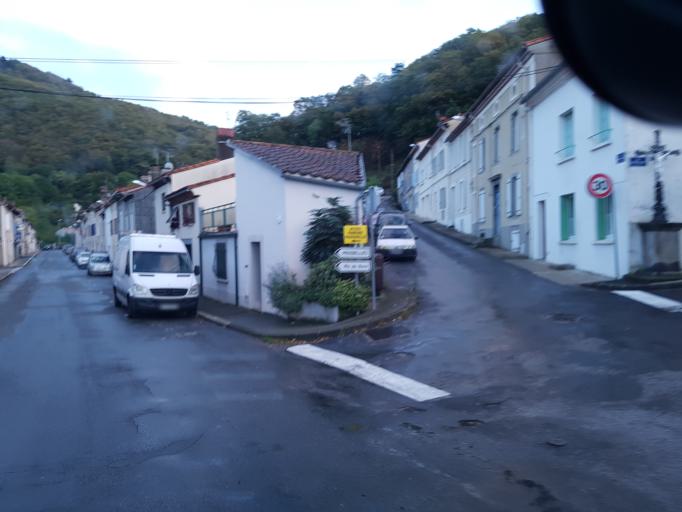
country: FR
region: Midi-Pyrenees
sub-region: Departement du Tarn
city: Mazamet
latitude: 43.4838
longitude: 2.3743
